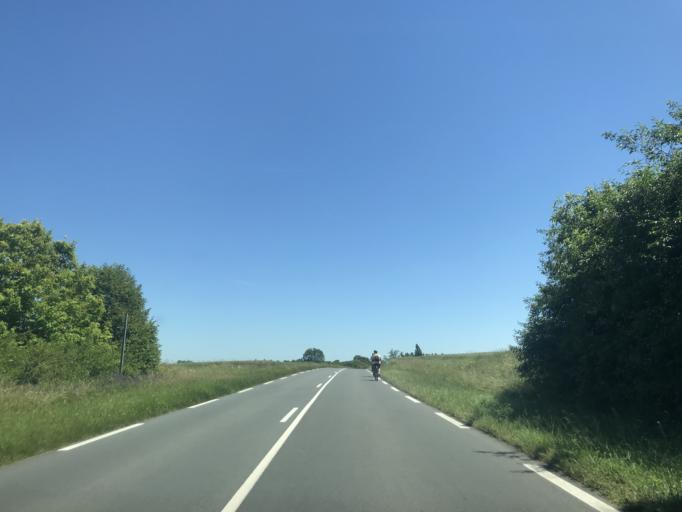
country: FR
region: Poitou-Charentes
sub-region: Departement de la Charente-Maritime
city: Meschers-sur-Gironde
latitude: 45.5541
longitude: -0.9197
